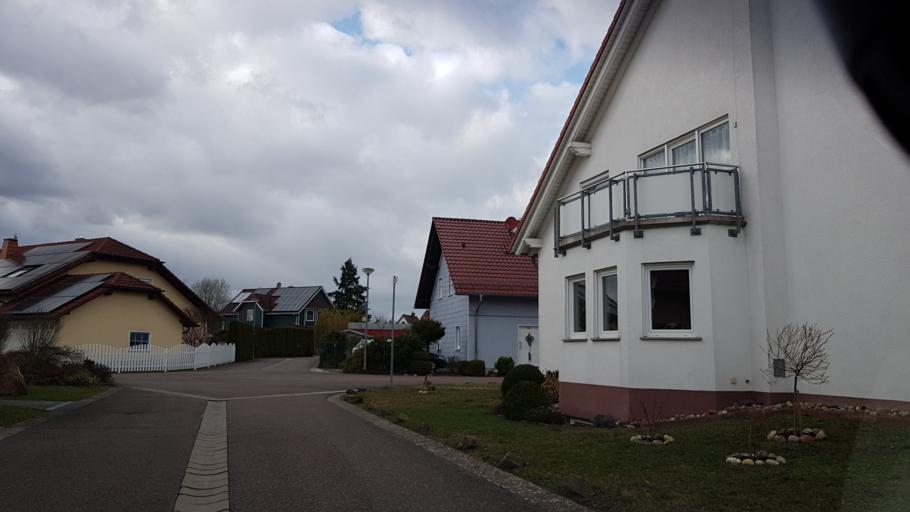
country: DE
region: Saarland
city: Bexbach
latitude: 49.3501
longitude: 7.2688
